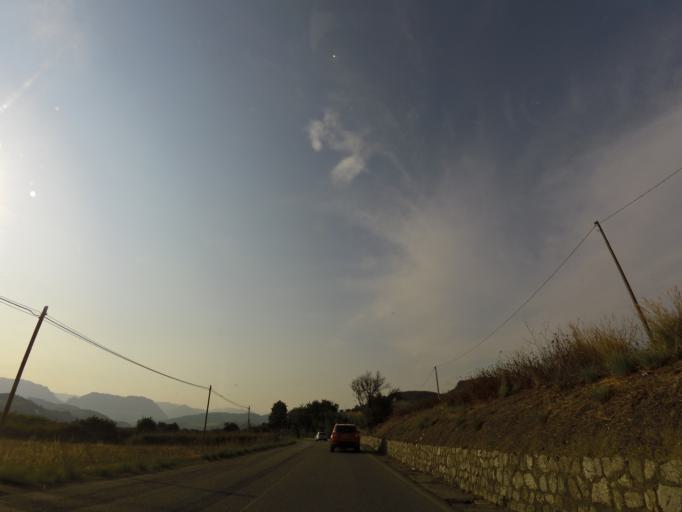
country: IT
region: Calabria
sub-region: Provincia di Reggio Calabria
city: Monasterace
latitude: 38.4473
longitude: 16.5341
